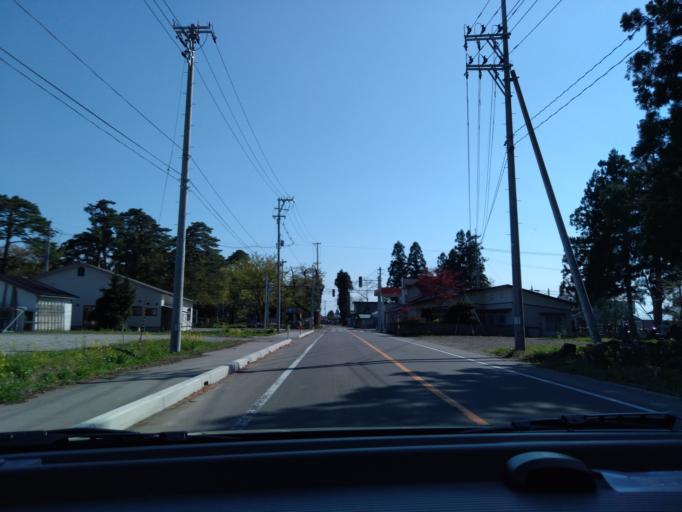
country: JP
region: Akita
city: Omagari
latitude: 39.4738
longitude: 140.5855
